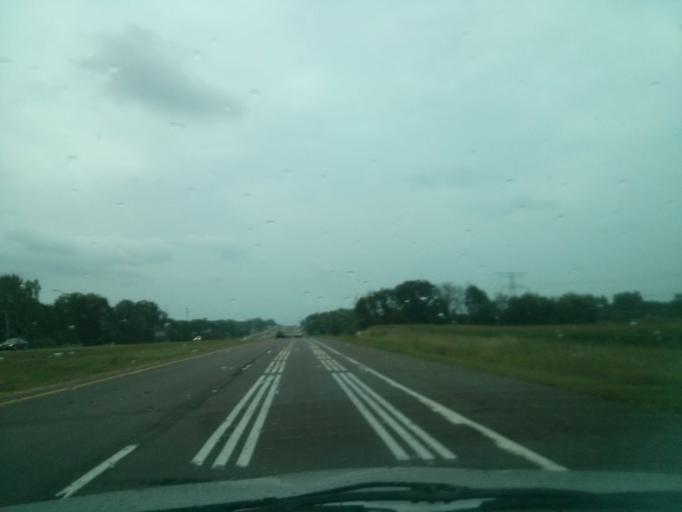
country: US
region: Minnesota
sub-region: Washington County
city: Lake Elmo
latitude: 45.0355
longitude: -92.8965
